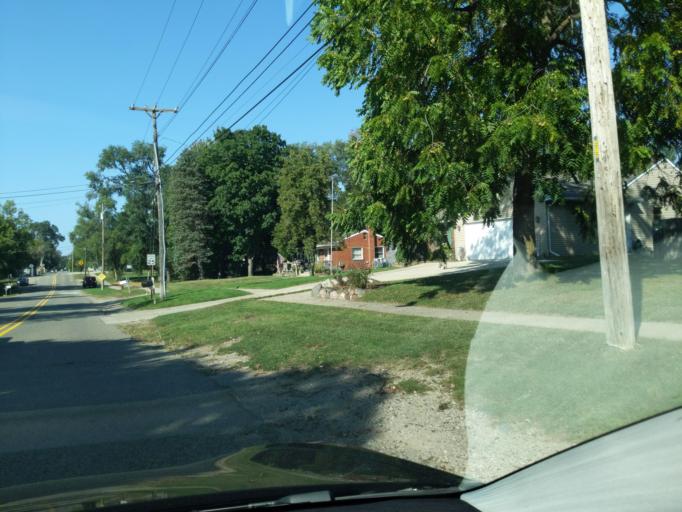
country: US
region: Michigan
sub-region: Oakland County
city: South Lyon
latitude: 42.4551
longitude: -83.6560
